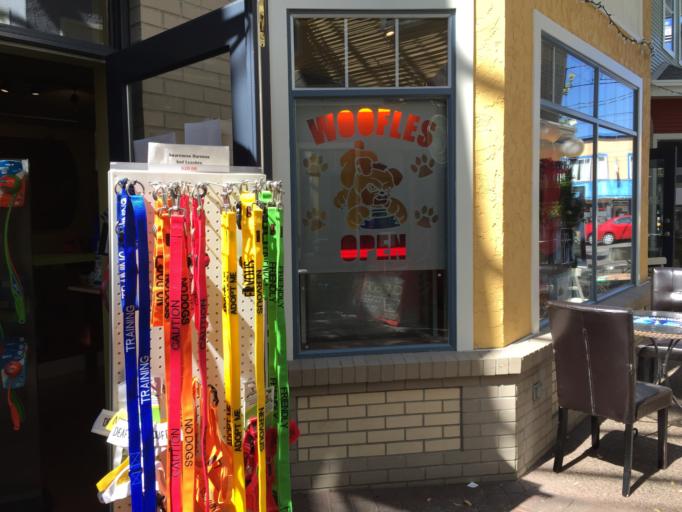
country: CA
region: British Columbia
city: Nanaimo
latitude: 49.1650
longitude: -123.9422
